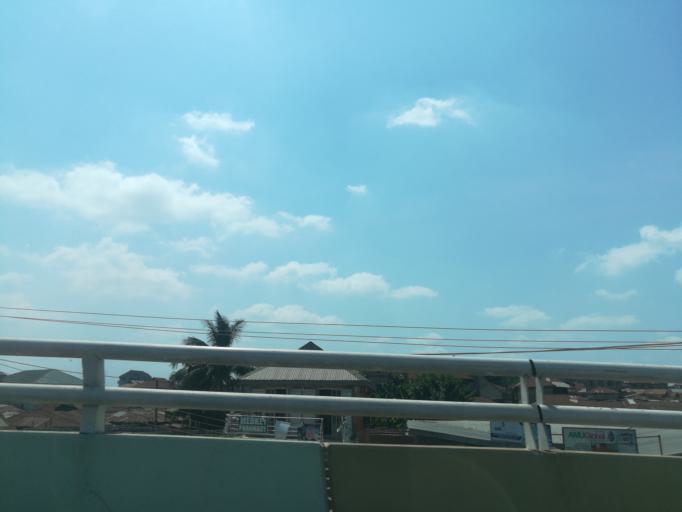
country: NG
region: Ogun
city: Abeokuta
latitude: 7.1552
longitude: 3.3458
